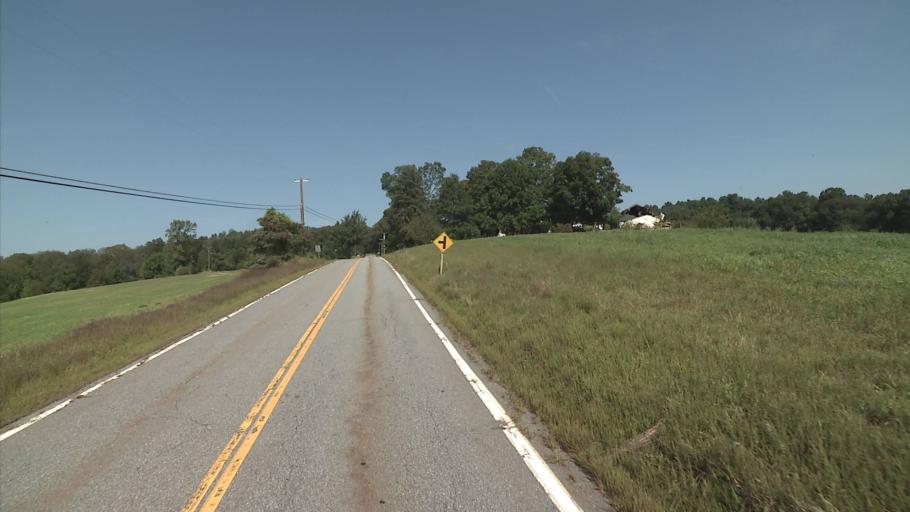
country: US
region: Connecticut
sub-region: Windham County
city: Quinebaug
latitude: 42.0163
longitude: -72.0059
